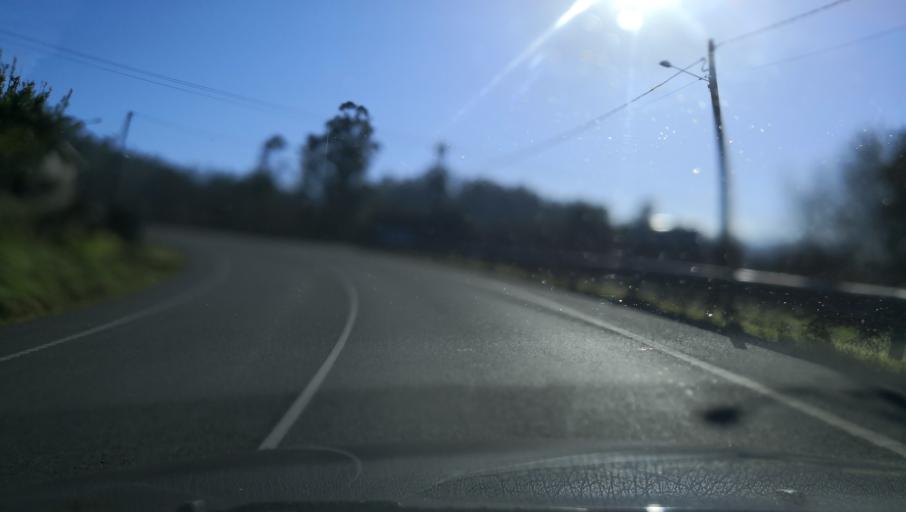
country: ES
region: Galicia
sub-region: Provincia da Coruna
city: Ribeira
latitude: 42.7567
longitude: -8.3947
